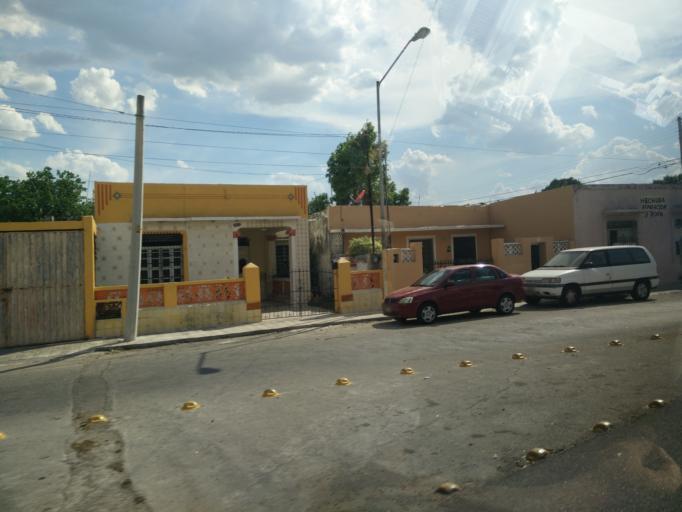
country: MX
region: Yucatan
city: Merida
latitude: 20.9647
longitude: -89.6063
